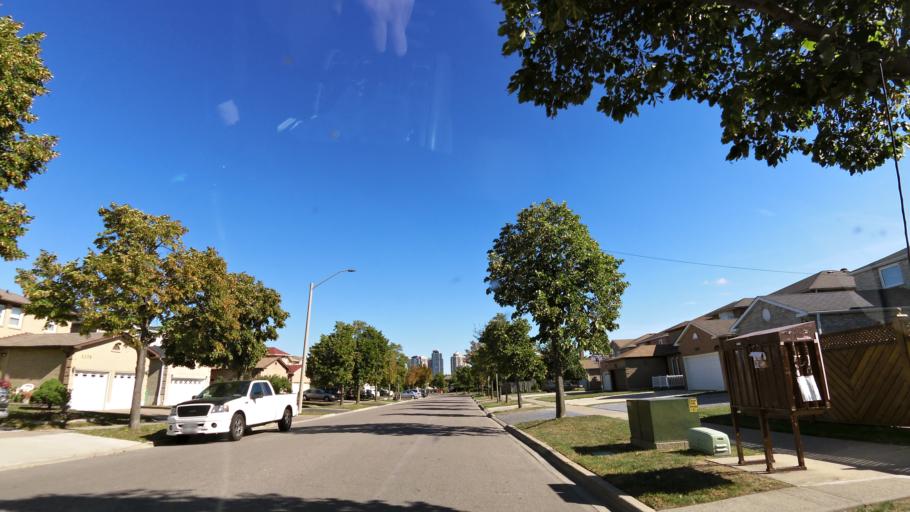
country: CA
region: Ontario
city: Mississauga
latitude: 43.6117
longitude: -79.6663
